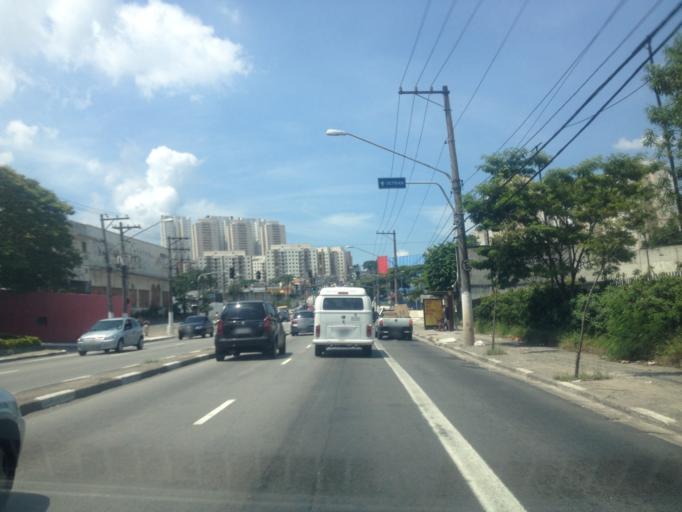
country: BR
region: Sao Paulo
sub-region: Diadema
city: Diadema
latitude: -23.6631
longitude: -46.6789
